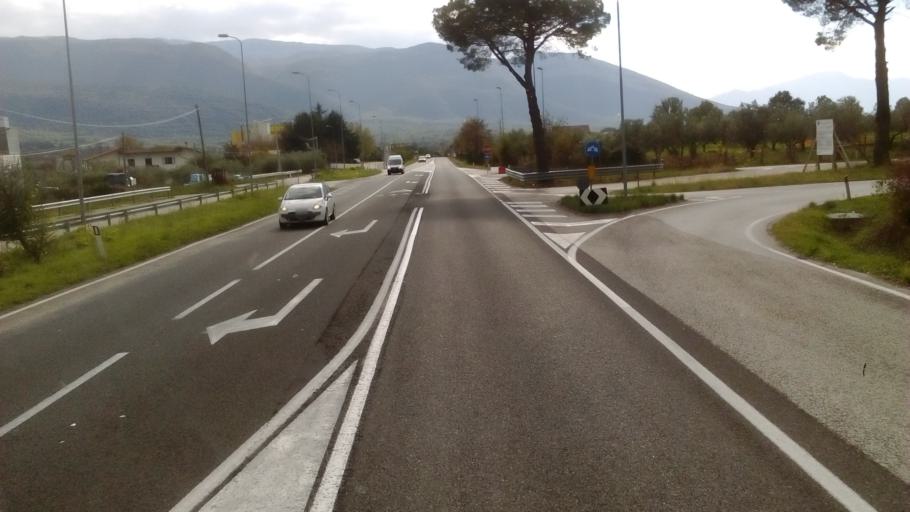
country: IT
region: Molise
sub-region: Provincia di Isernia
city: Macchia d'Isernia
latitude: 41.5410
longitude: 14.1581
